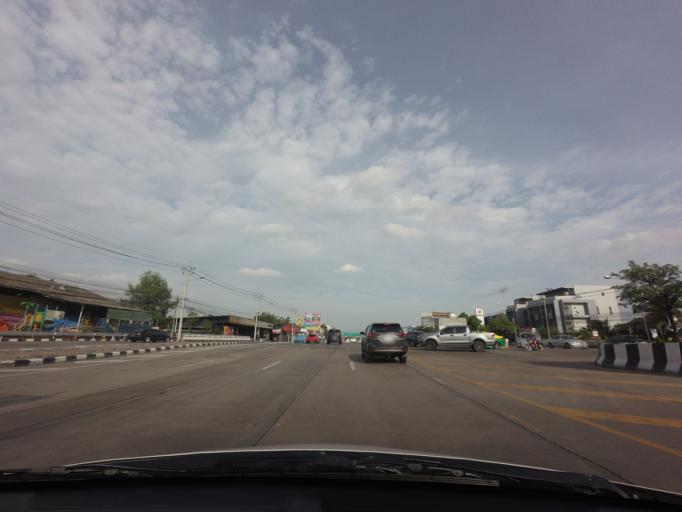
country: TH
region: Bangkok
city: Bueng Kum
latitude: 13.8119
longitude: 100.6477
